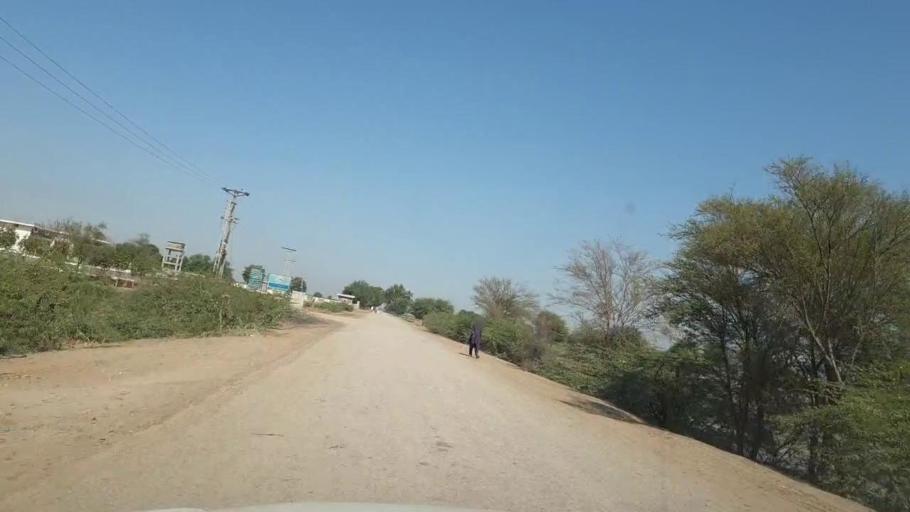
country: PK
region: Sindh
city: Kunri
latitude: 25.1300
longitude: 69.5094
